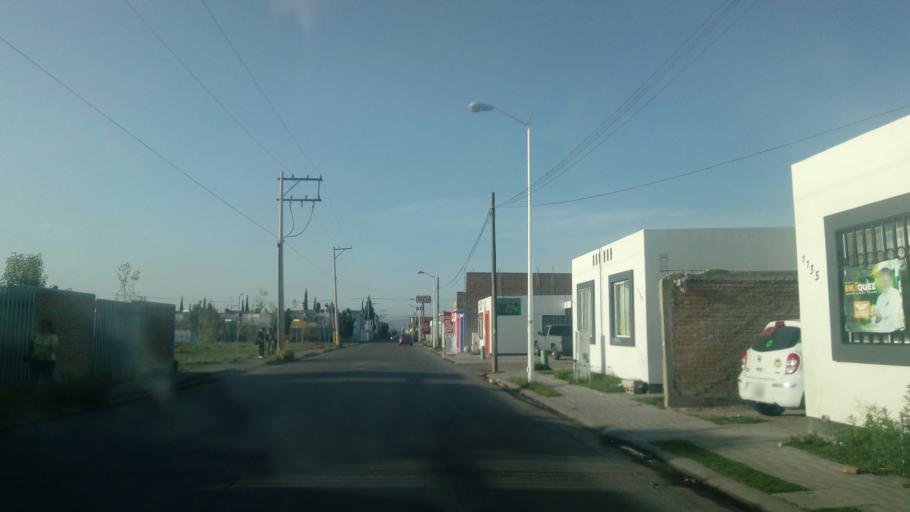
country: MX
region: Durango
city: Victoria de Durango
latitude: 24.0729
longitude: -104.5899
